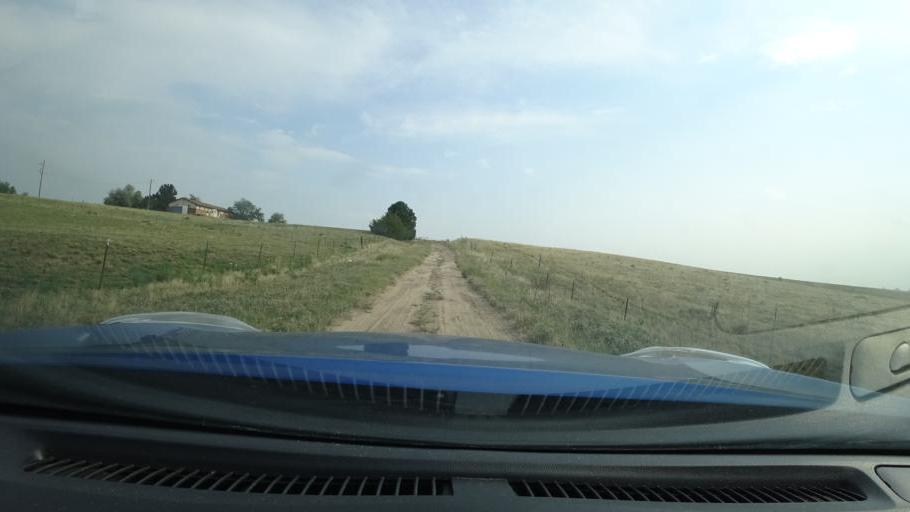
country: US
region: Colorado
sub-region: Adams County
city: Aurora
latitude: 39.7305
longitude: -104.7442
